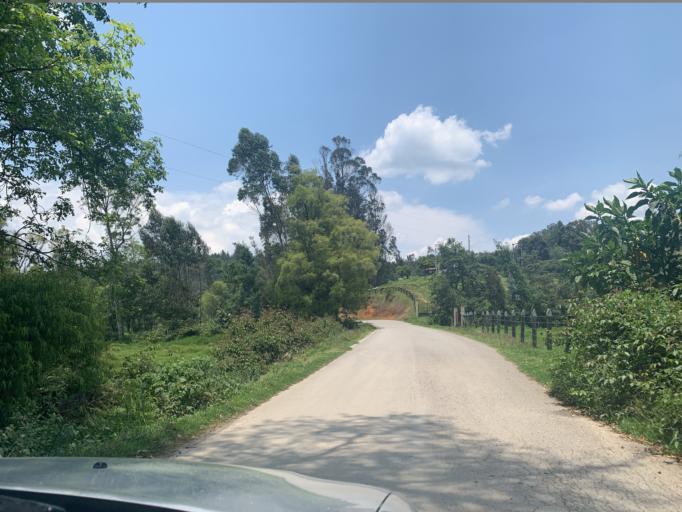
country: CO
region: Boyaca
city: Chiquinquira
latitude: 5.5731
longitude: -73.7463
